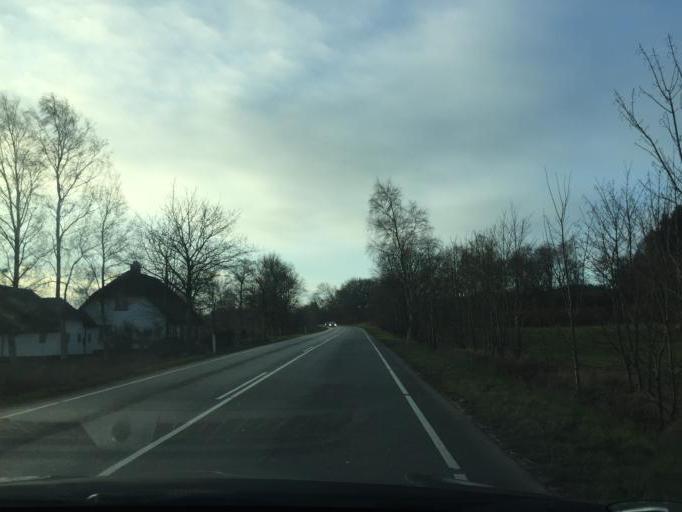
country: DK
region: South Denmark
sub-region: Faaborg-Midtfyn Kommune
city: Faaborg
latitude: 55.1576
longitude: 10.2706
